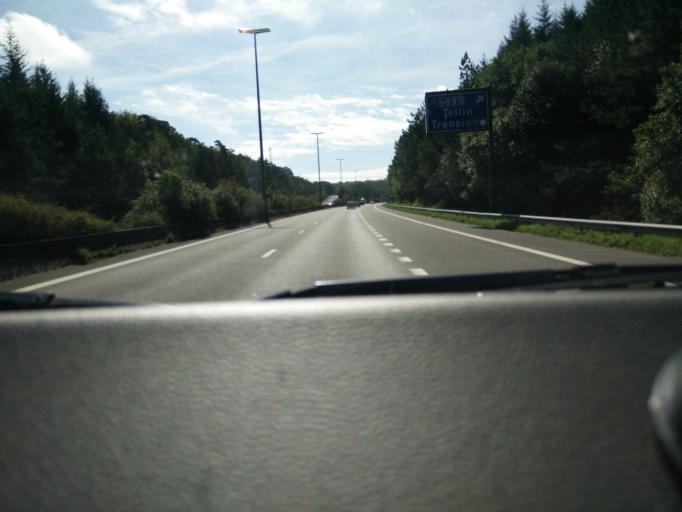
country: BE
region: Wallonia
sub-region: Province du Luxembourg
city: Tellin
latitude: 50.0572
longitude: 5.2055
